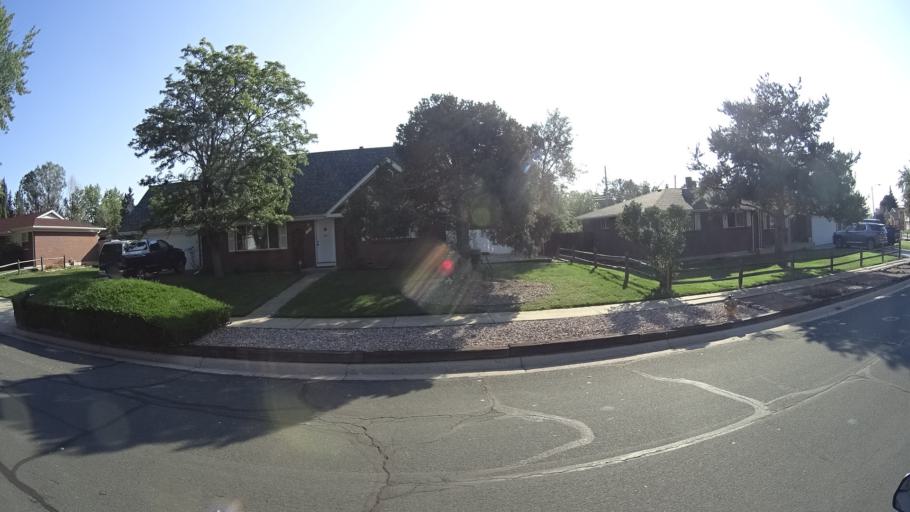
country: US
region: Colorado
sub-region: El Paso County
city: Colorado Springs
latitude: 38.8900
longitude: -104.8366
